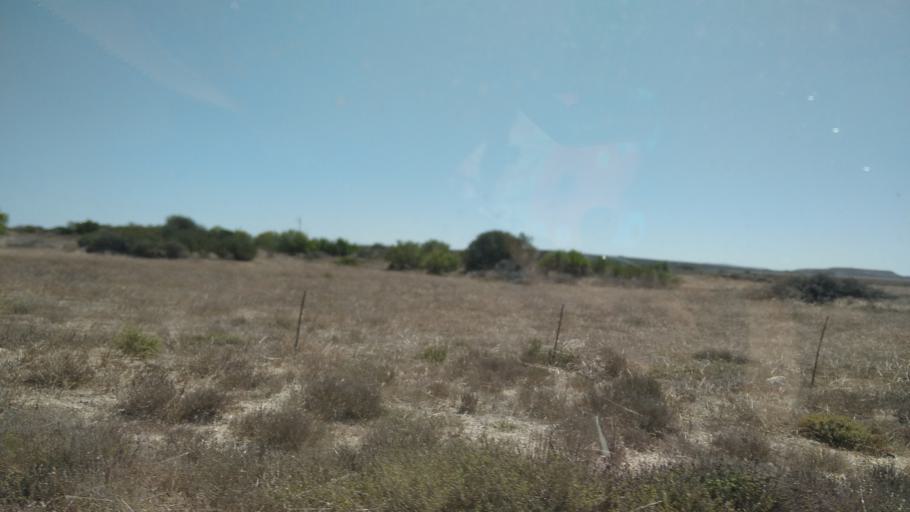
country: ZA
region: Western Cape
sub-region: West Coast District Municipality
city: Vredenburg
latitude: -32.9931
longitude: 18.1327
